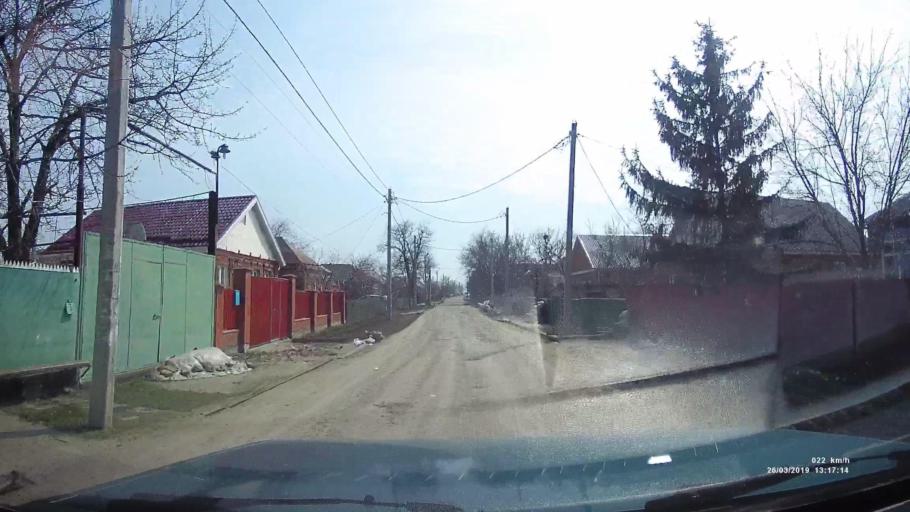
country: RU
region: Rostov
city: Novobessergenovka
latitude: 47.1723
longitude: 38.7668
